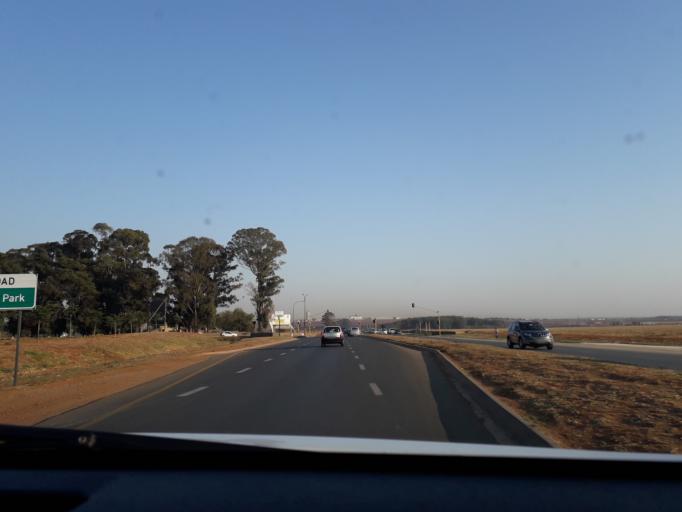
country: ZA
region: Gauteng
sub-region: Ekurhuleni Metropolitan Municipality
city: Tembisa
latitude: -26.0580
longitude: 28.2747
